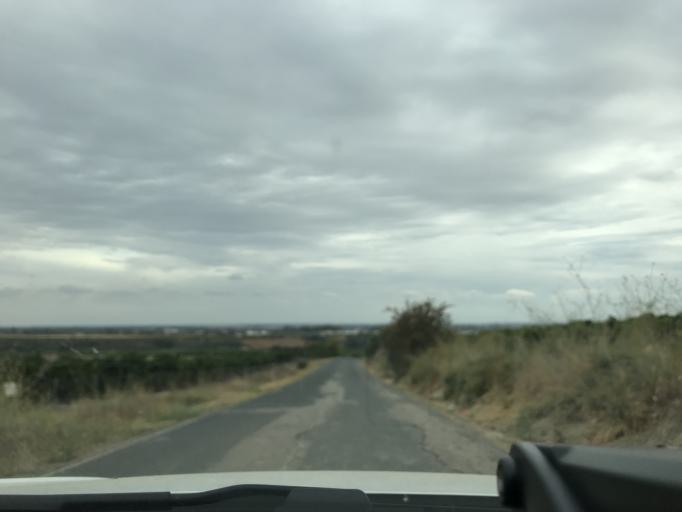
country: ES
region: Andalusia
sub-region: Provincia de Sevilla
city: Villanueva del Rio y Minas
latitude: 37.6391
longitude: -5.7029
